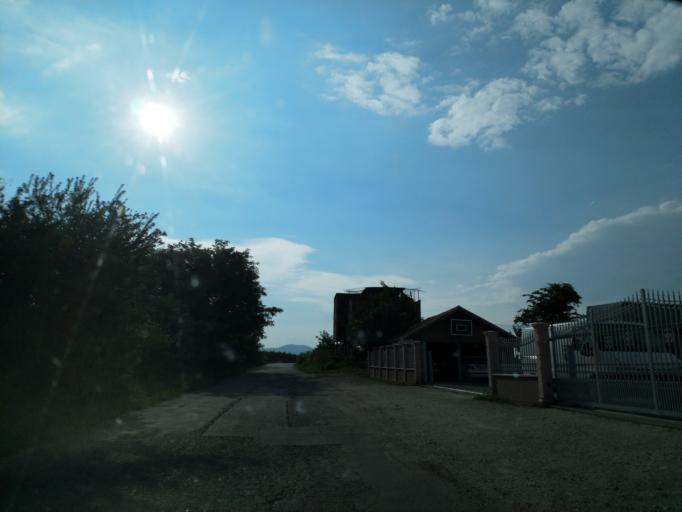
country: RS
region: Central Serbia
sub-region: Pomoravski Okrug
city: Jagodina
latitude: 43.9785
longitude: 21.2323
